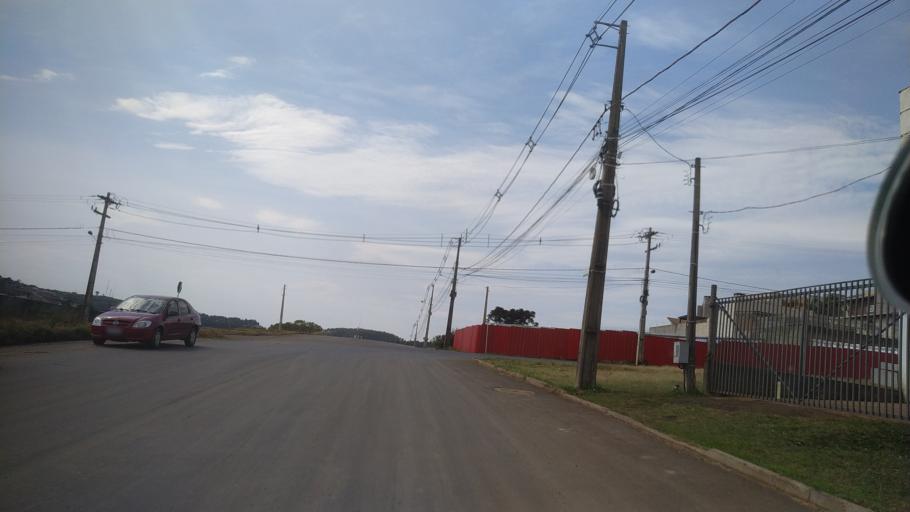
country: BR
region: Santa Catarina
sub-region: Chapeco
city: Chapeco
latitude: -27.1321
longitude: -52.6062
